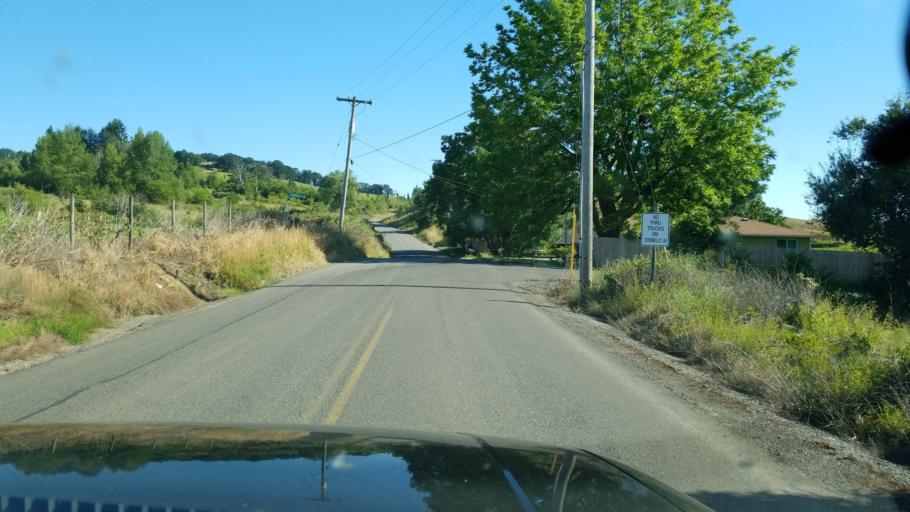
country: US
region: Oregon
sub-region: Yamhill County
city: McMinnville
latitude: 45.2449
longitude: -123.2307
